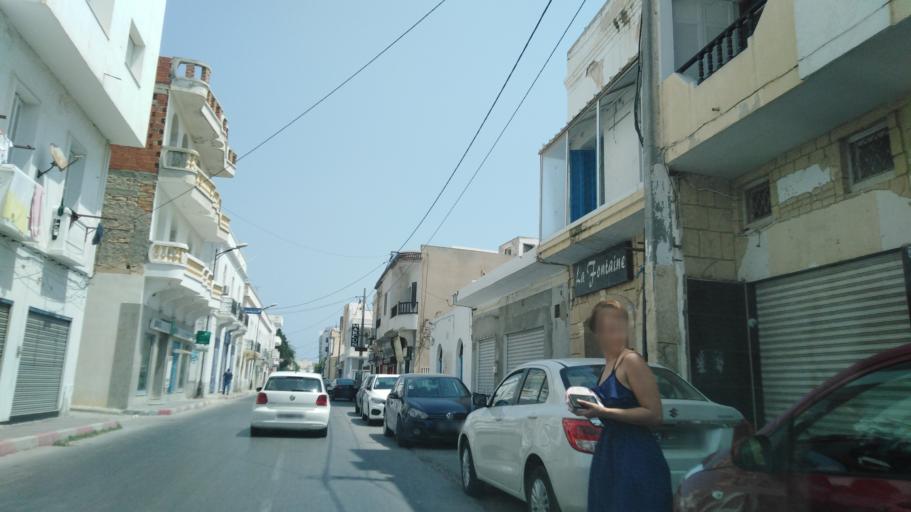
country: TN
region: Al Mahdiyah
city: Mahdia
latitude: 35.5065
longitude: 11.0595
